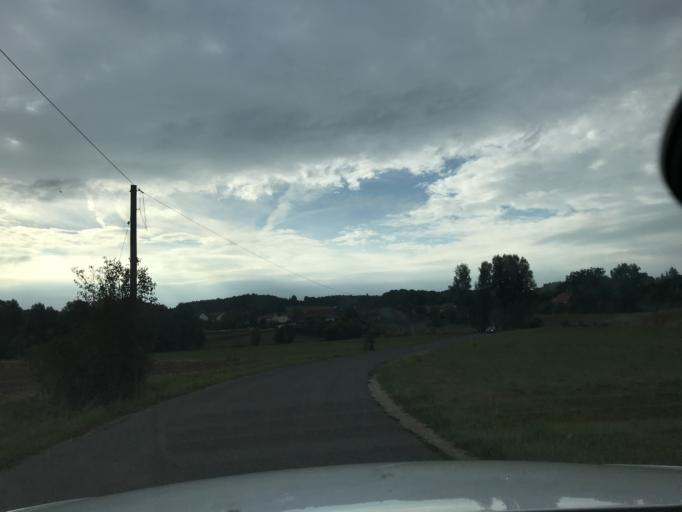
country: DE
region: Bavaria
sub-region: Upper Franconia
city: Pegnitz
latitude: 49.7485
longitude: 11.5543
